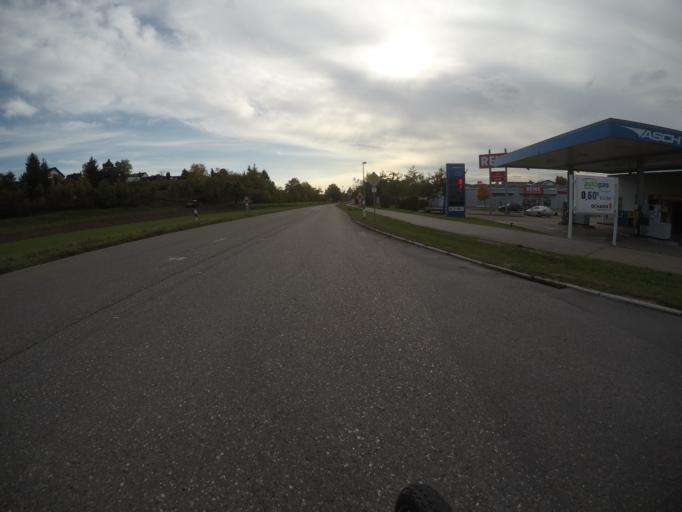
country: DE
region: Baden-Wuerttemberg
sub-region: Regierungsbezirk Stuttgart
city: Herrenberg
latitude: 48.5649
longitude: 8.9090
